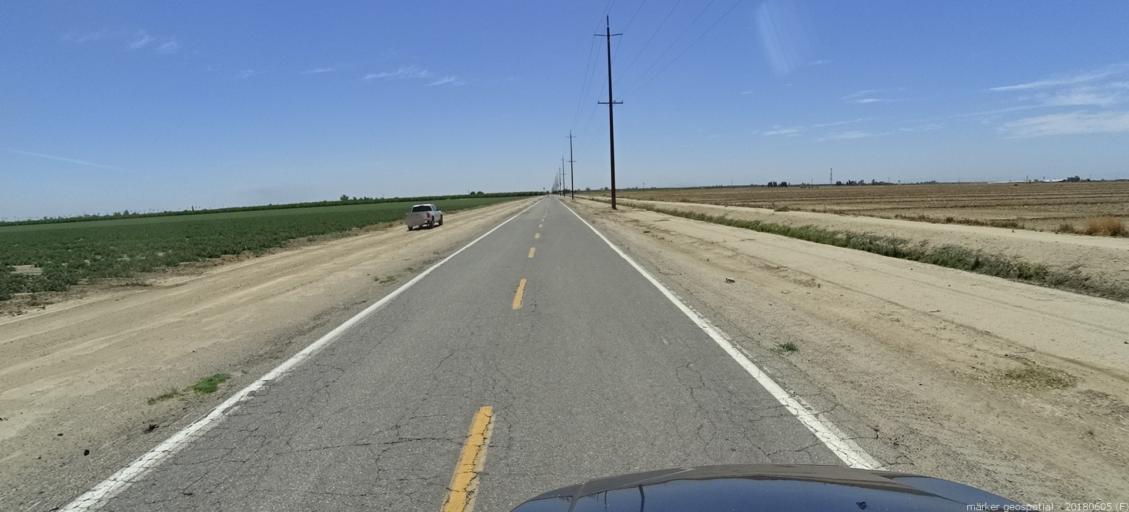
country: US
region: California
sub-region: Madera County
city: Chowchilla
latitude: 37.1039
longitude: -120.3109
